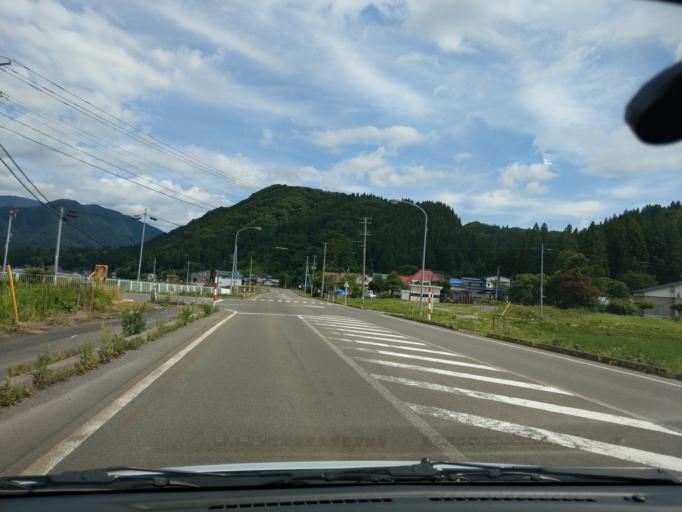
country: JP
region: Akita
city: Kakunodatemachi
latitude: 39.6751
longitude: 140.5657
